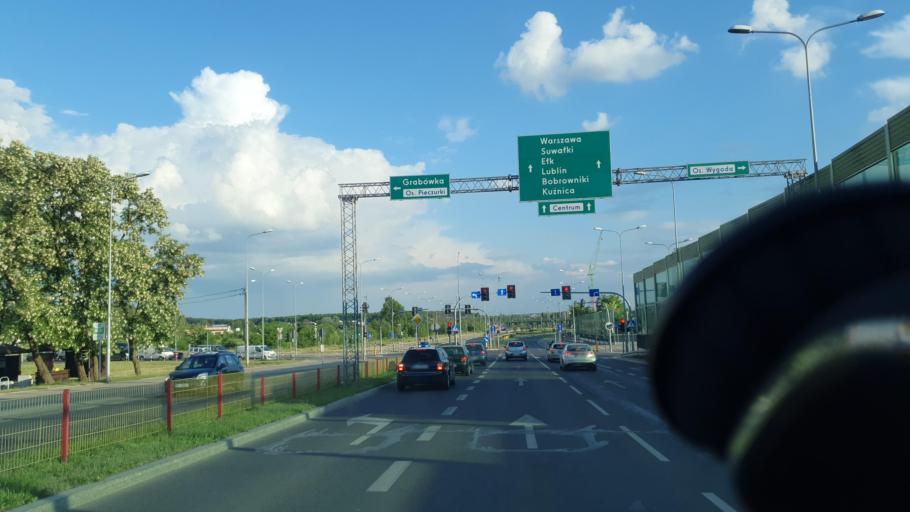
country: PL
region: Podlasie
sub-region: Bialystok
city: Bialystok
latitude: 53.1448
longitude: 23.2018
